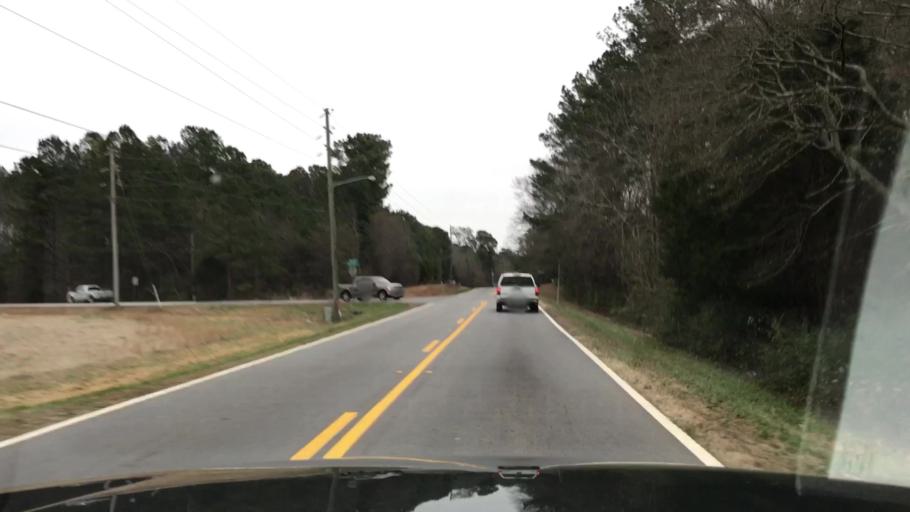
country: US
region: Georgia
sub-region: Walton County
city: Monroe
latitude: 33.8598
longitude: -83.7415
